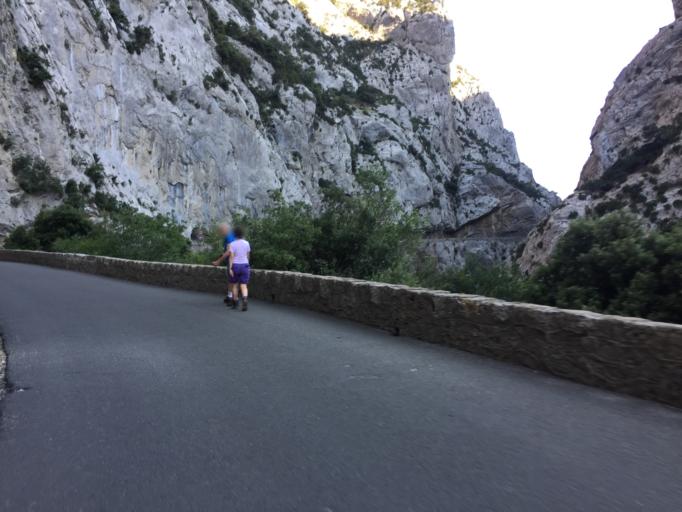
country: FR
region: Languedoc-Roussillon
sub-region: Departement des Pyrenees-Orientales
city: Saint-Paul-de-Fenouillet
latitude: 42.8437
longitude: 2.4792
